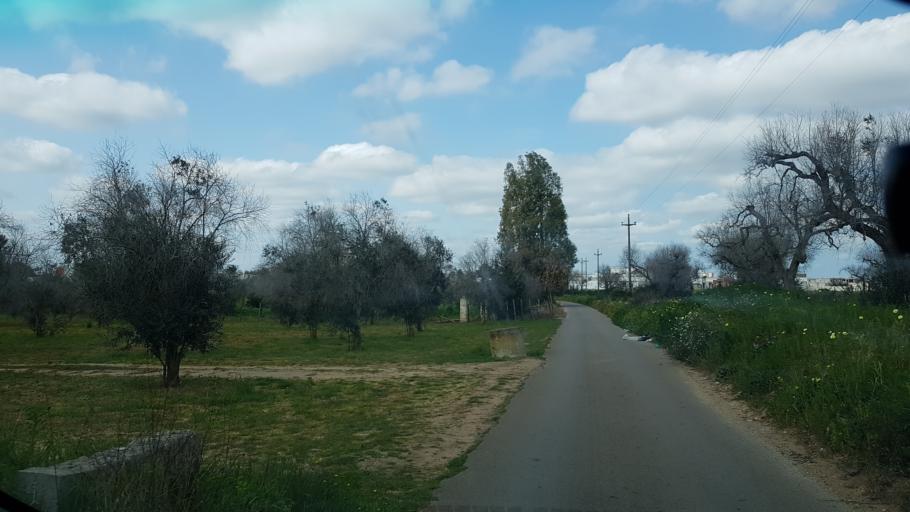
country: IT
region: Apulia
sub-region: Provincia di Brindisi
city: Torchiarolo
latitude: 40.4790
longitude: 18.0607
